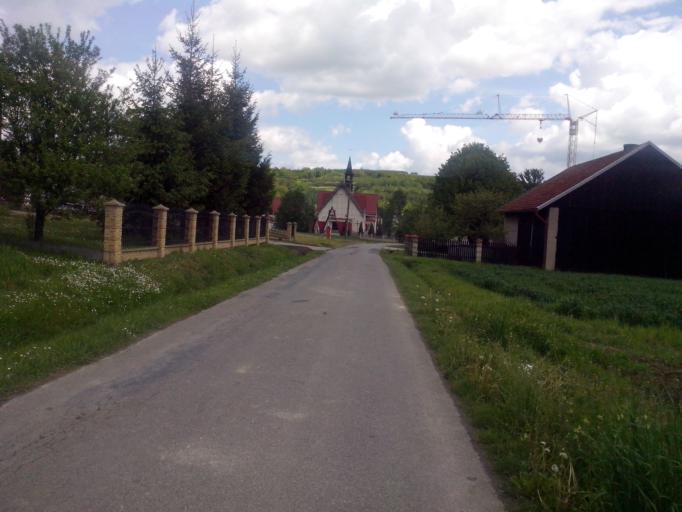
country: PL
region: Subcarpathian Voivodeship
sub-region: Powiat strzyzowski
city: Strzyzow
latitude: 49.8436
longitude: 21.8098
